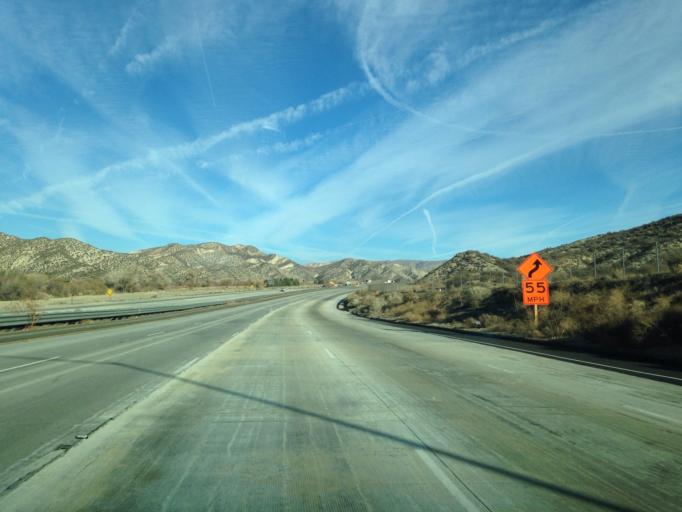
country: US
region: California
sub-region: Kern County
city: Lebec
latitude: 34.7108
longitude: -118.7973
